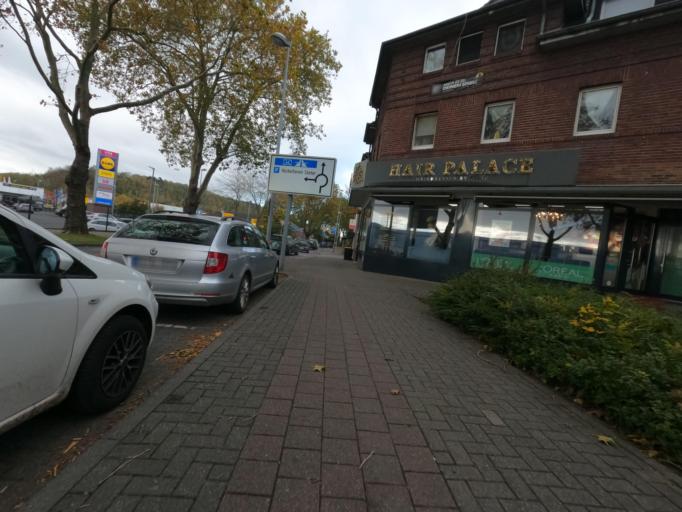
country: DE
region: North Rhine-Westphalia
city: Huckelhoven
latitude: 51.0572
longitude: 6.2208
